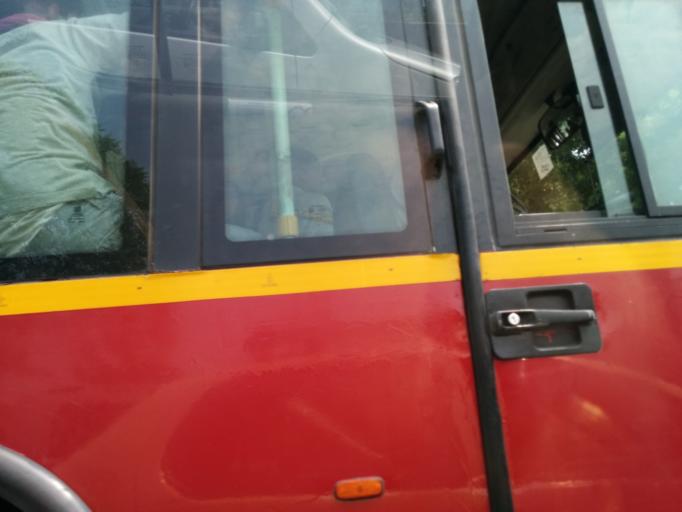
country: IN
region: NCT
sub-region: New Delhi
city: New Delhi
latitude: 28.5439
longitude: 77.2040
